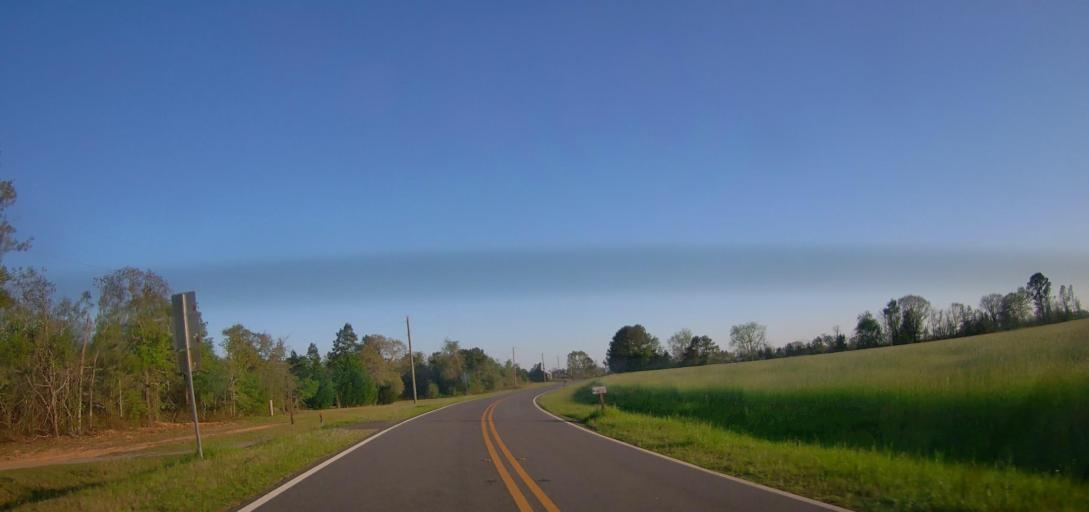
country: US
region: Georgia
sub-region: Marion County
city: Buena Vista
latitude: 32.4590
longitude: -84.4257
